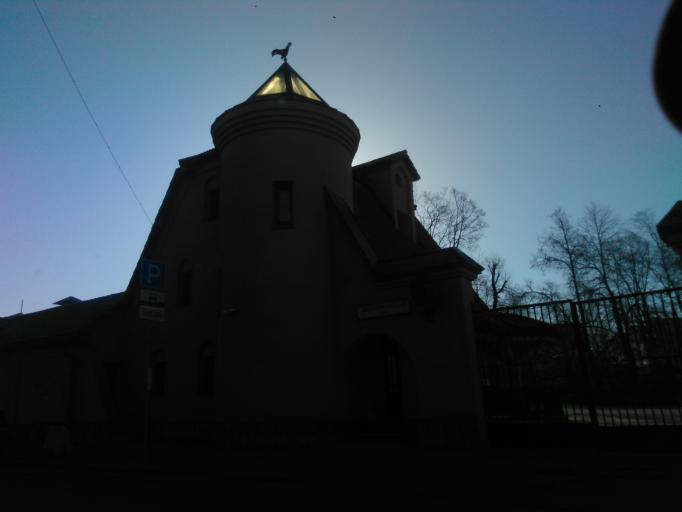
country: RU
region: Moskovskaya
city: Dorogomilovo
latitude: 55.7642
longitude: 37.5823
